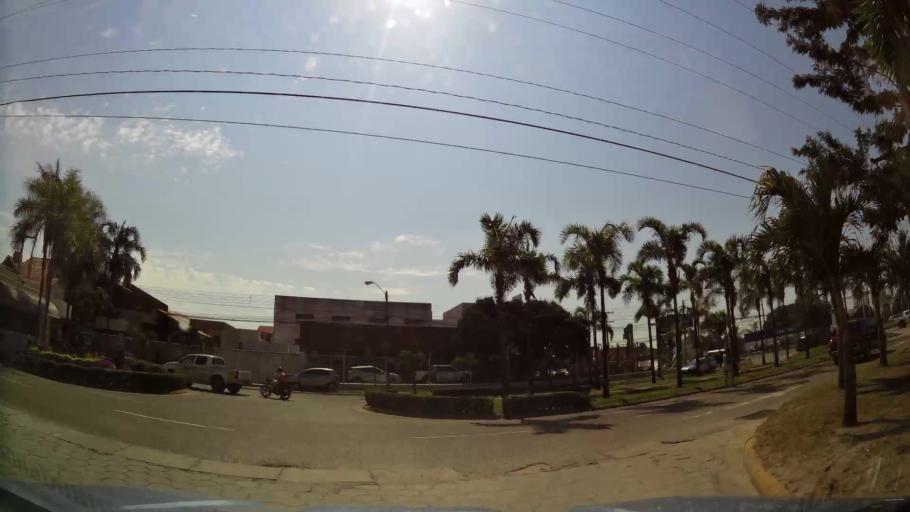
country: BO
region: Santa Cruz
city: Santa Cruz de la Sierra
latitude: -17.7482
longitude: -63.1752
